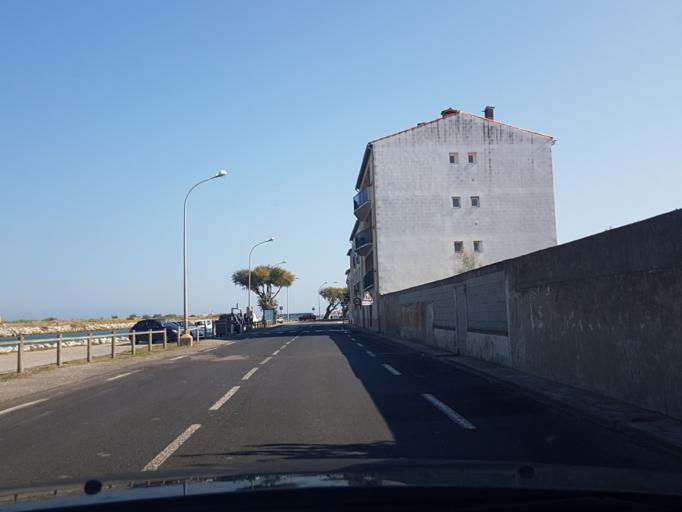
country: FR
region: Languedoc-Roussillon
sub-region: Departement de l'Aude
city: Port-la-Nouvelle
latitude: 43.0187
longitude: 3.0571
